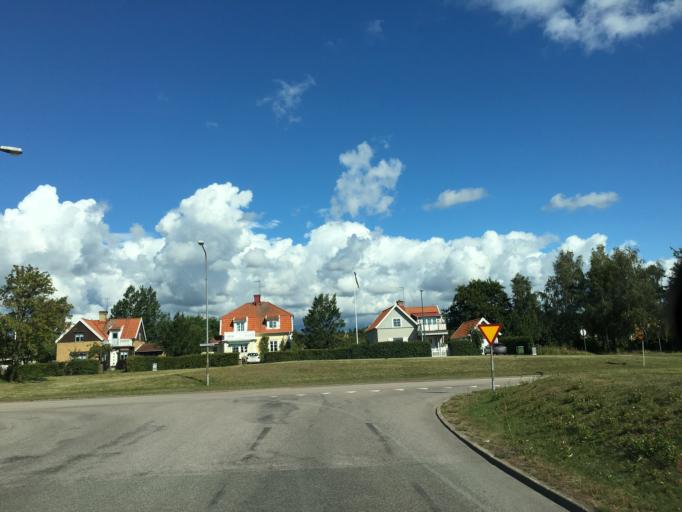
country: SE
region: Kalmar
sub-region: Kalmar Kommun
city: Kalmar
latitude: 56.6742
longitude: 16.3546
